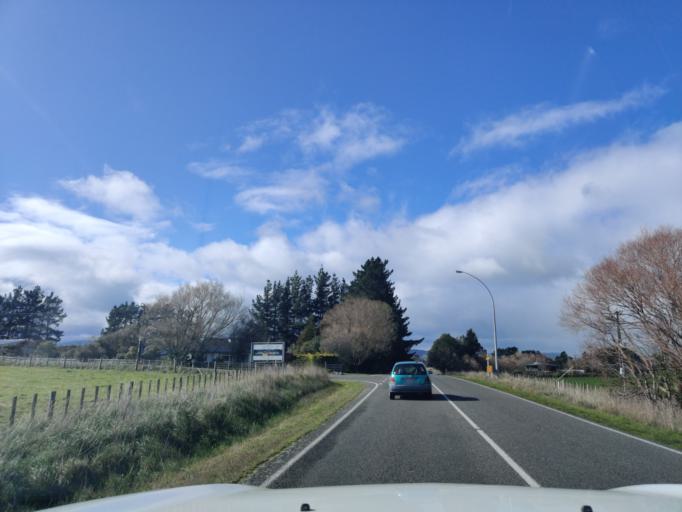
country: NZ
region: Manawatu-Wanganui
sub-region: Palmerston North City
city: Palmerston North
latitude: -40.2885
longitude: 175.6962
